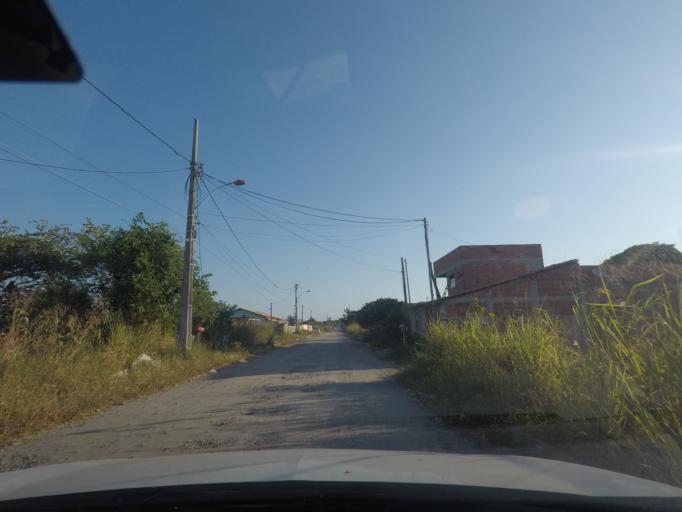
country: BR
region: Rio de Janeiro
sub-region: Marica
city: Marica
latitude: -22.9625
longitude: -42.9326
